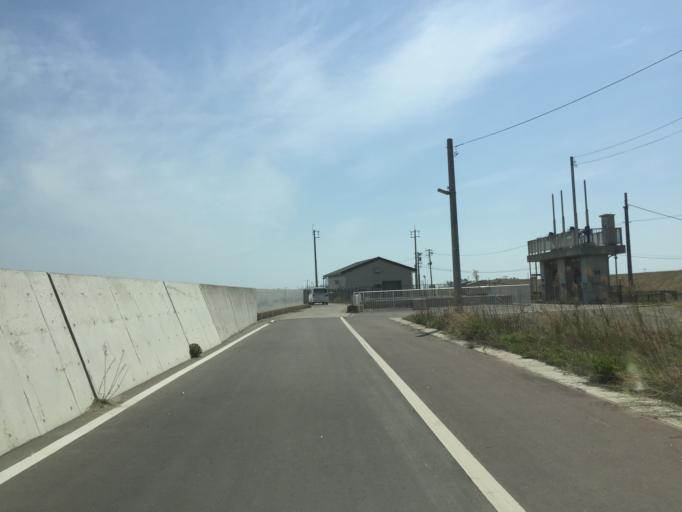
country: JP
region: Miyagi
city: Watari
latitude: 38.0313
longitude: 140.9022
